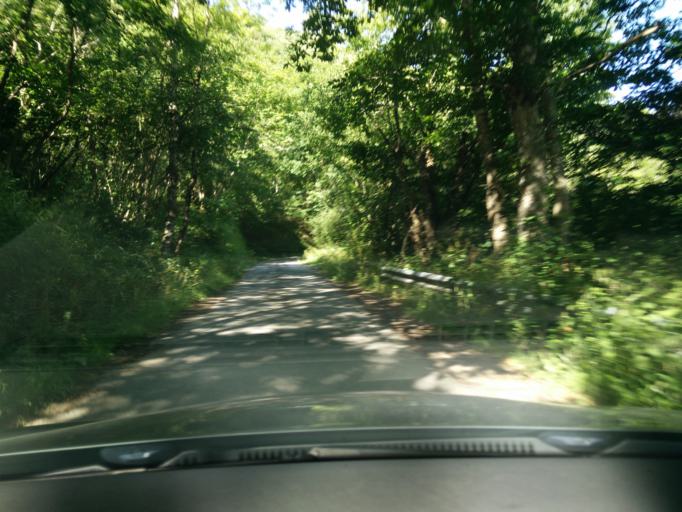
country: ES
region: Asturias
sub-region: Province of Asturias
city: Amieva
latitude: 43.1835
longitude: -5.1613
